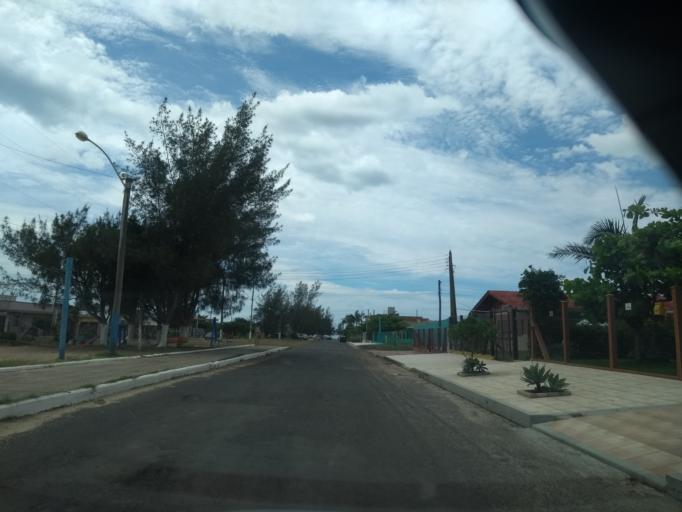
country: BR
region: Rio Grande do Sul
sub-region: Tramandai
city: Tramandai
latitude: -30.0621
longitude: -50.1637
